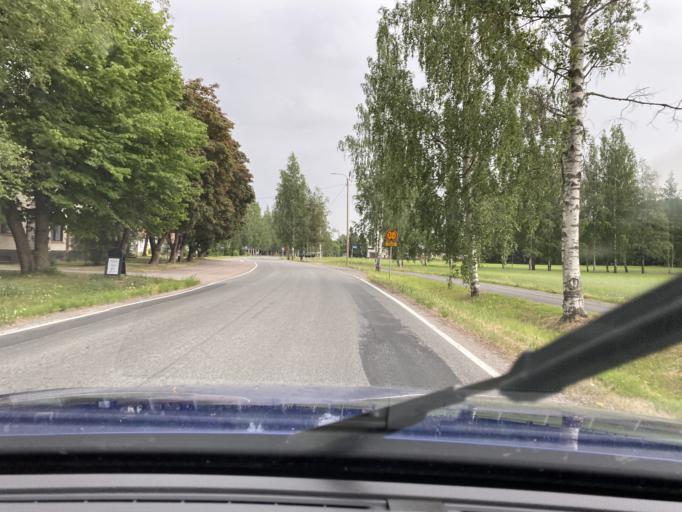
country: FI
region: Satakunta
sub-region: Rauma
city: Eura
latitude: 61.1376
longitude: 22.1253
